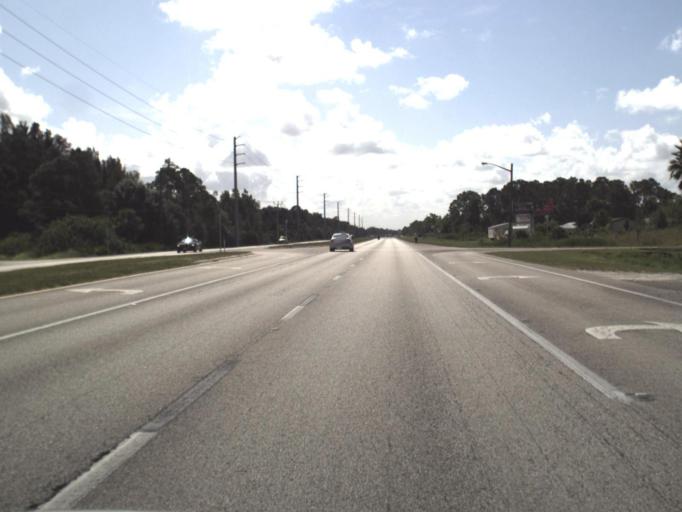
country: US
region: Florida
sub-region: Charlotte County
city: Charlotte Park
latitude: 26.8686
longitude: -82.0000
